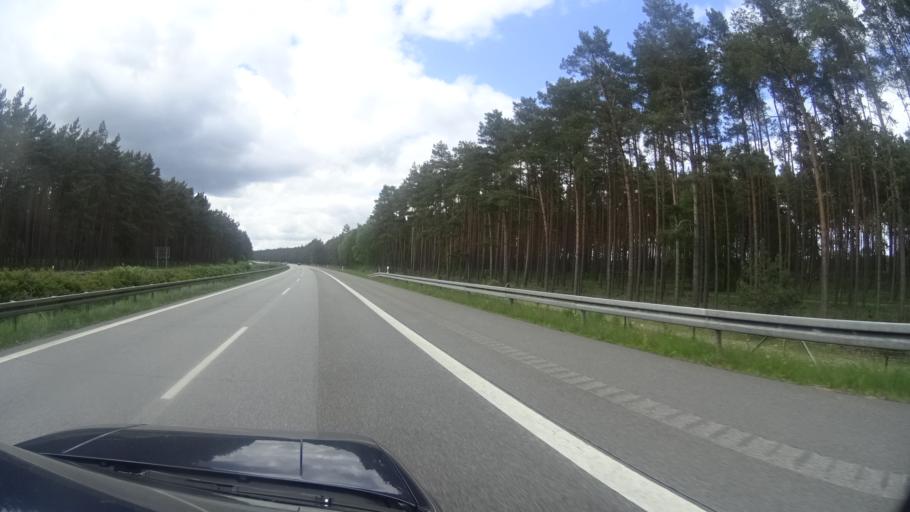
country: DE
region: Mecklenburg-Vorpommern
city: Malchow
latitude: 53.5323
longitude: 12.3510
